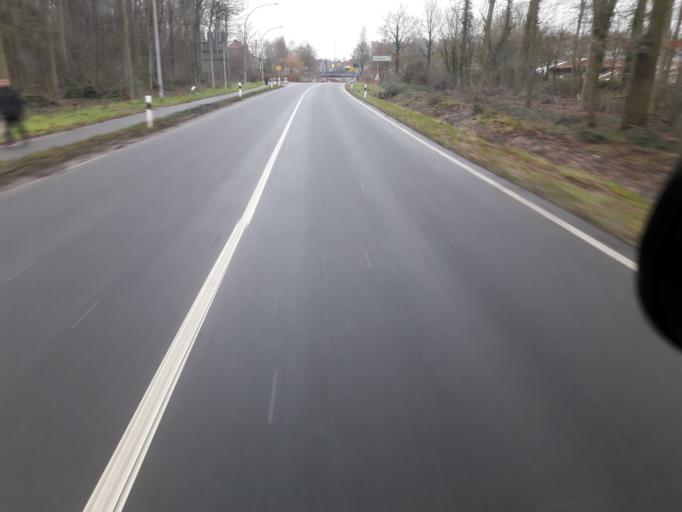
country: DE
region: Lower Saxony
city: Bad Bentheim
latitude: 52.3127
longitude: 7.1589
